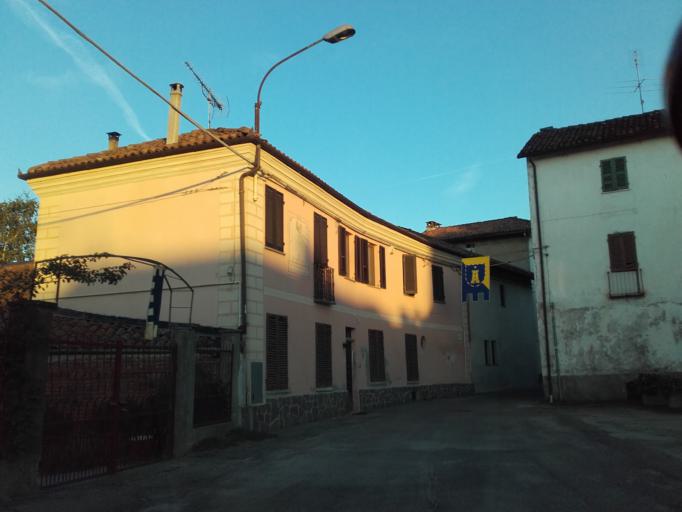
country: IT
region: Piedmont
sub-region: Provincia di Asti
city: Mongardino
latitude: 44.8629
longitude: 8.2142
